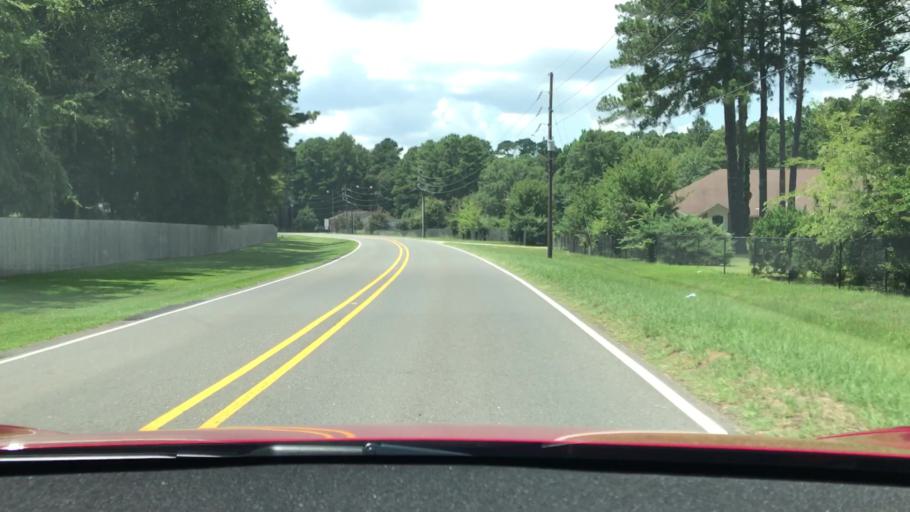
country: US
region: Louisiana
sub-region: De Soto Parish
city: Stonewall
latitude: 32.3678
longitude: -93.7016
